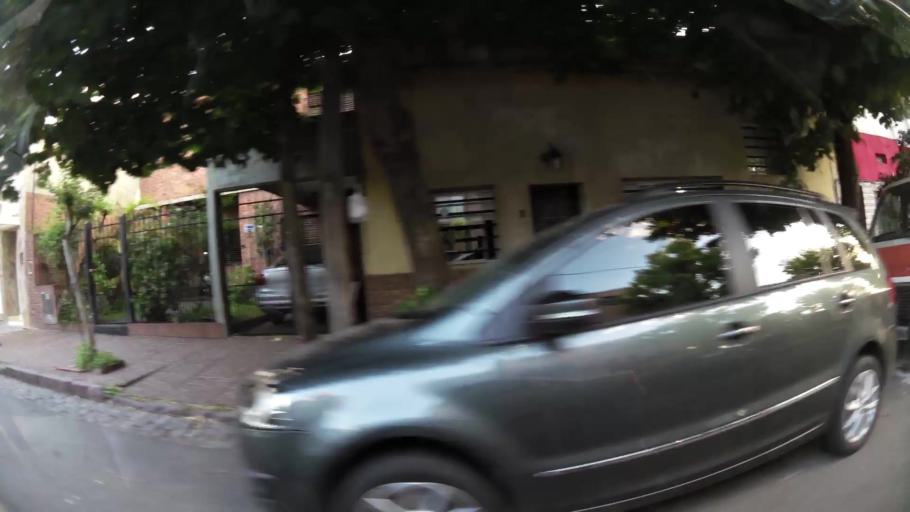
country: AR
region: Buenos Aires
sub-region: Partido de Vicente Lopez
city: Olivos
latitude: -34.5402
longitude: -58.5028
